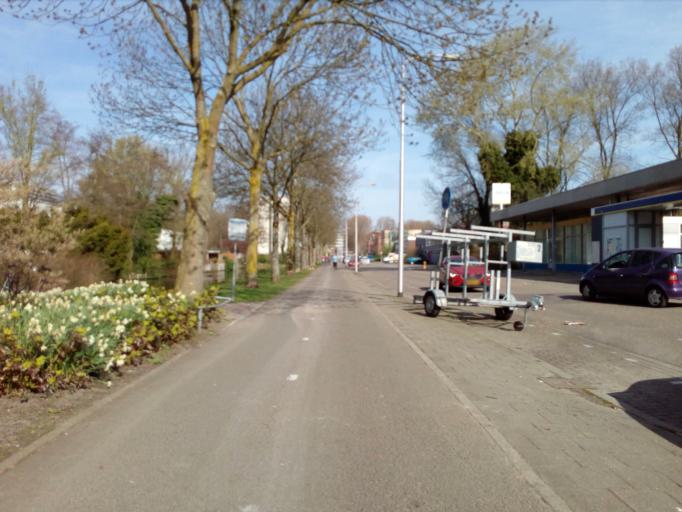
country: NL
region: South Holland
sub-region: Gemeente Delft
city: Delft
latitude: 51.9942
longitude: 4.3614
